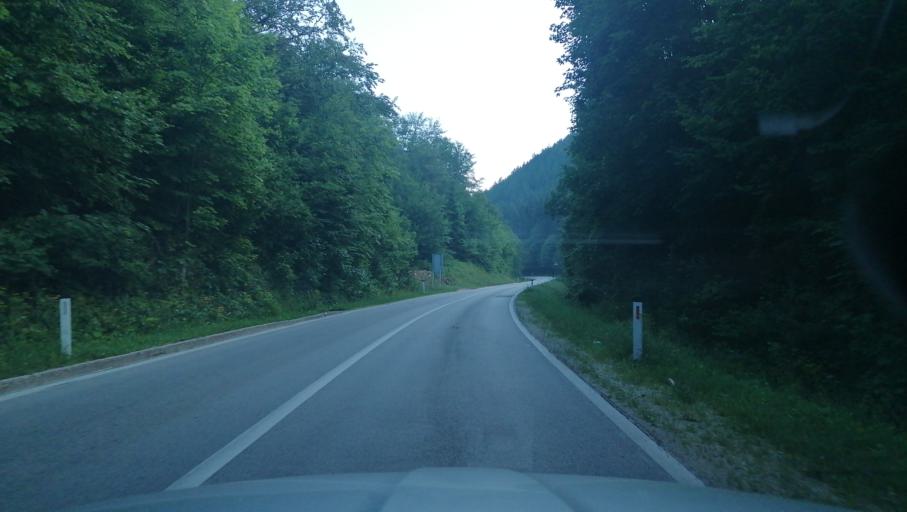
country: BA
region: Federation of Bosnia and Herzegovina
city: Prozor
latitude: 43.8719
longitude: 17.5935
